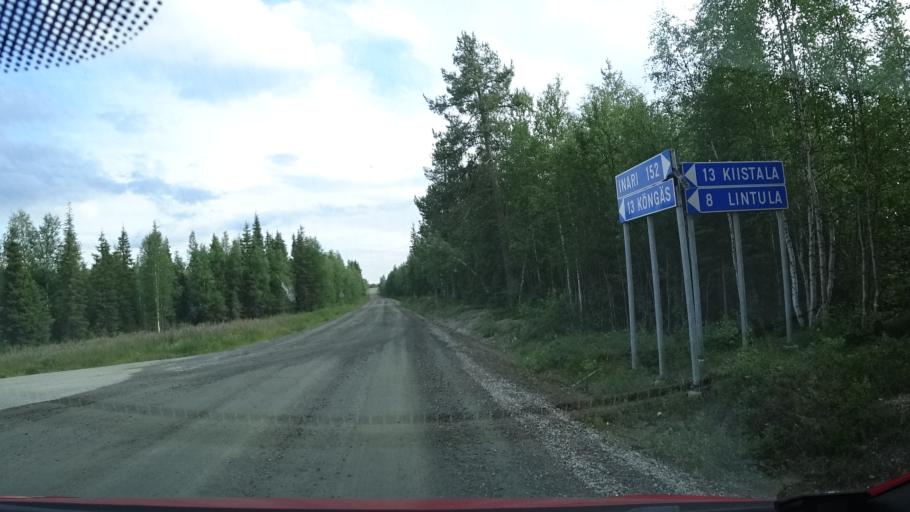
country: FI
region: Lapland
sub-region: Tunturi-Lappi
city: Kittilae
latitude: 67.9040
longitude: 25.0856
